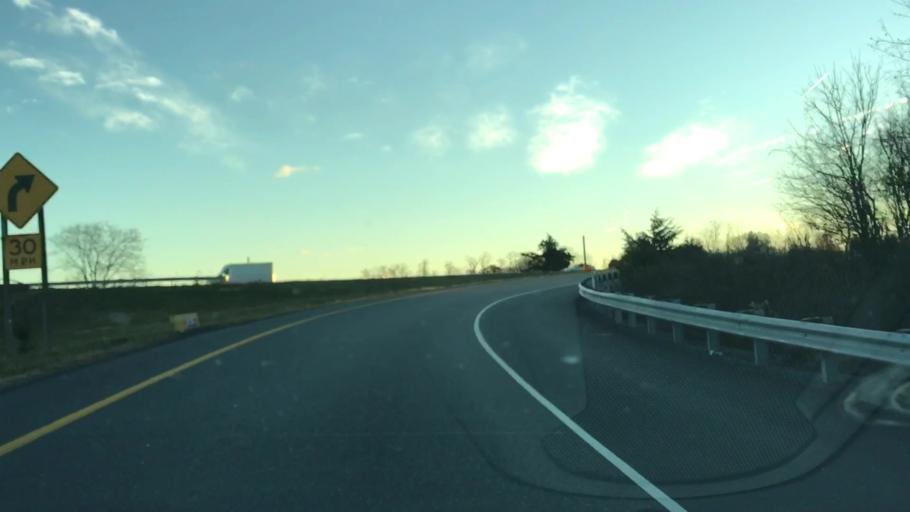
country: US
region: Pennsylvania
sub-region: Dauphin County
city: Paxtonia
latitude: 40.3254
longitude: -76.7921
